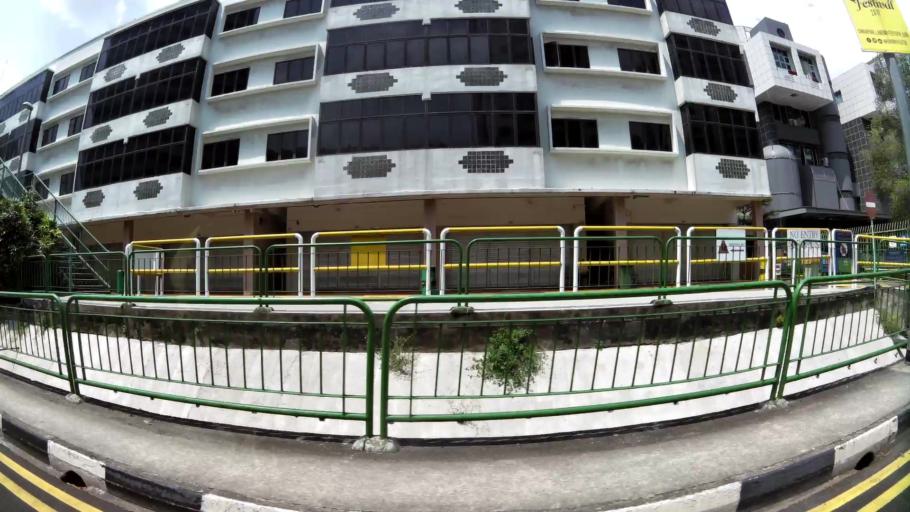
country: SG
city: Singapore
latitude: 1.2937
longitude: 103.8269
